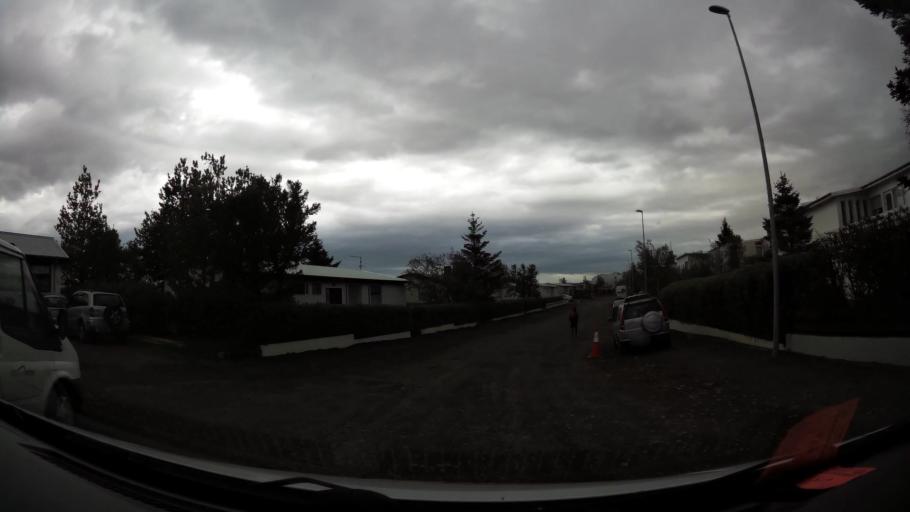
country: IS
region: West
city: Borgarnes
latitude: 64.5441
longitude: -21.9139
